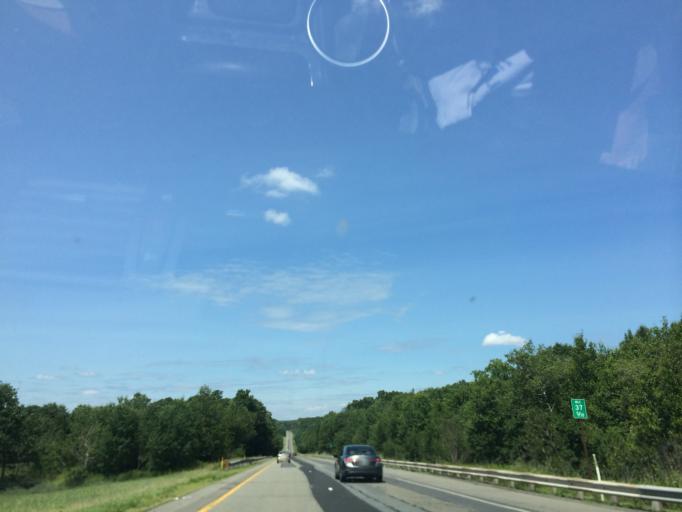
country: US
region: Pennsylvania
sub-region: Pike County
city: Conashaugh Lakes
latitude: 41.3468
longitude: -74.9979
